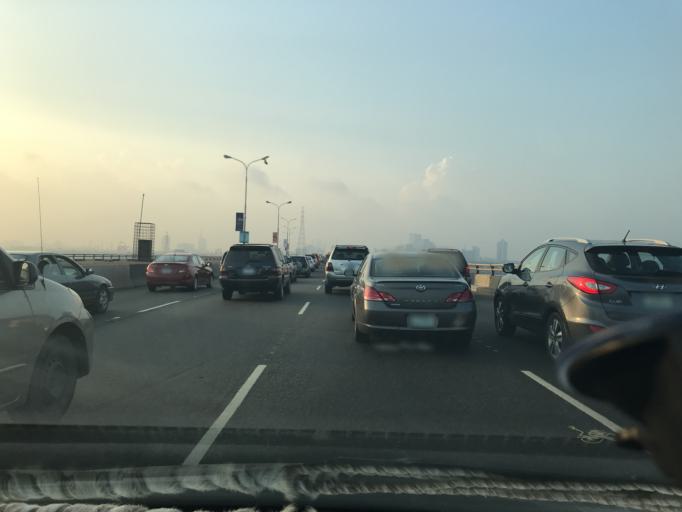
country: NG
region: Lagos
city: Ebute Metta
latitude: 6.4734
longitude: 3.3901
